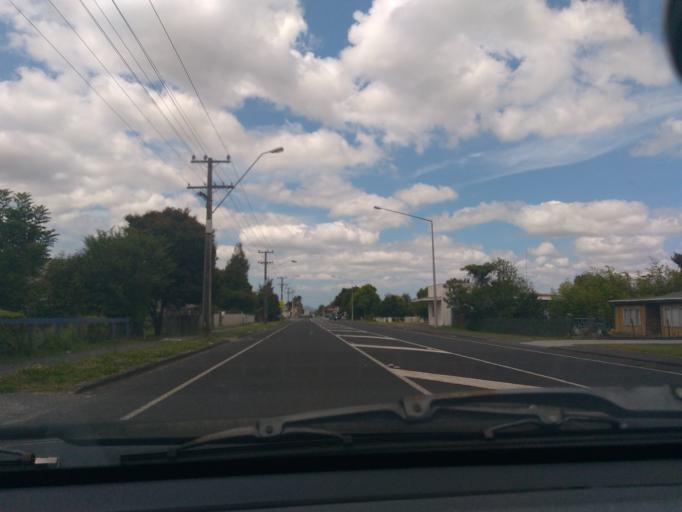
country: NZ
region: Northland
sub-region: Far North District
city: Moerewa
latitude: -35.3888
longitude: 174.0113
